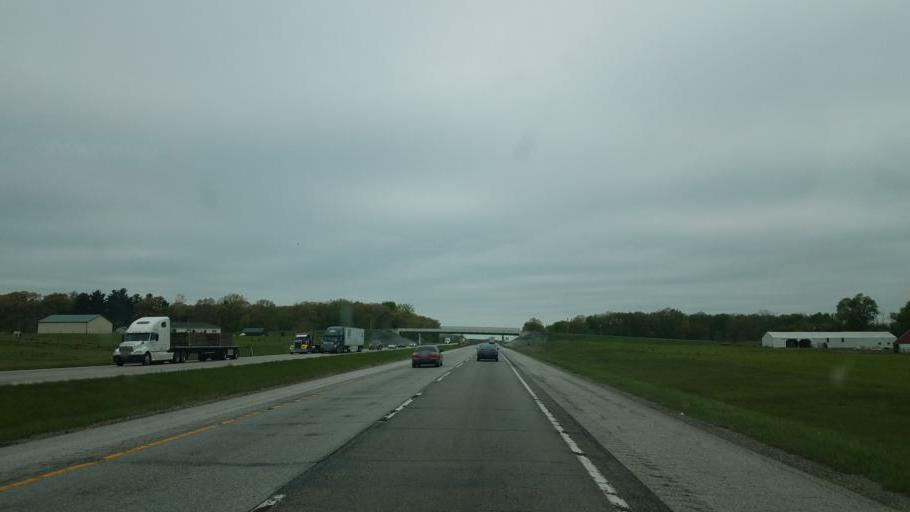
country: US
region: Michigan
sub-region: Saint Joseph County
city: White Pigeon
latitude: 41.7526
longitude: -85.5979
